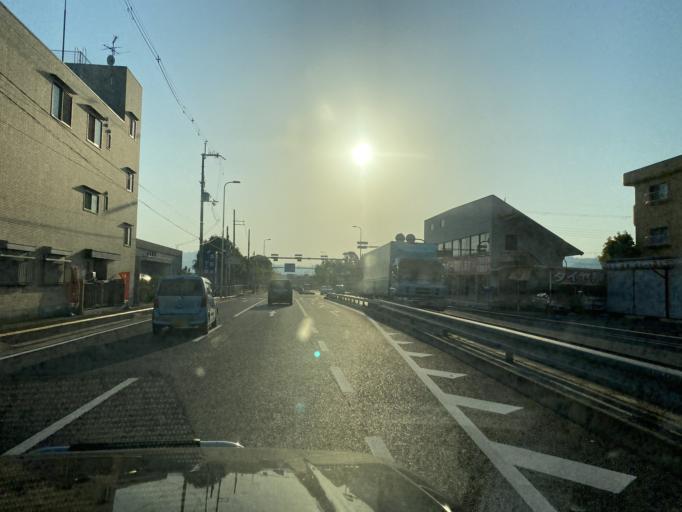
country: JP
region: Osaka
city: Ikeda
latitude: 34.8109
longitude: 135.4359
